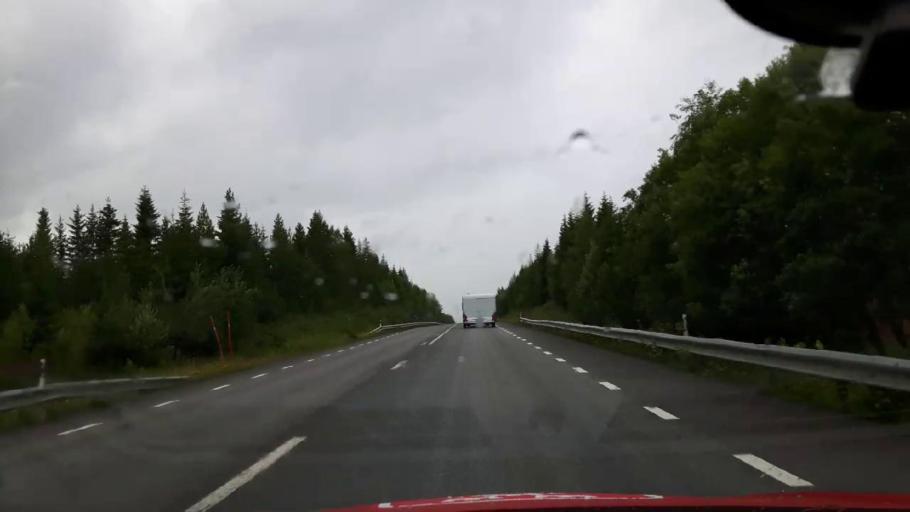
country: SE
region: Jaemtland
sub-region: Are Kommun
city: Jarpen
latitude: 63.3206
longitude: 13.5549
